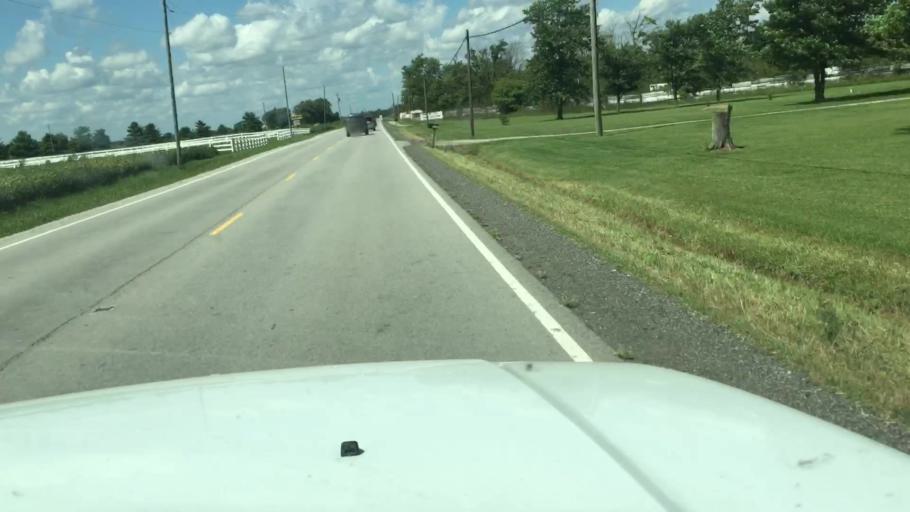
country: US
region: Ohio
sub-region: Madison County
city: Mount Sterling
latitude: 39.7438
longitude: -83.2812
